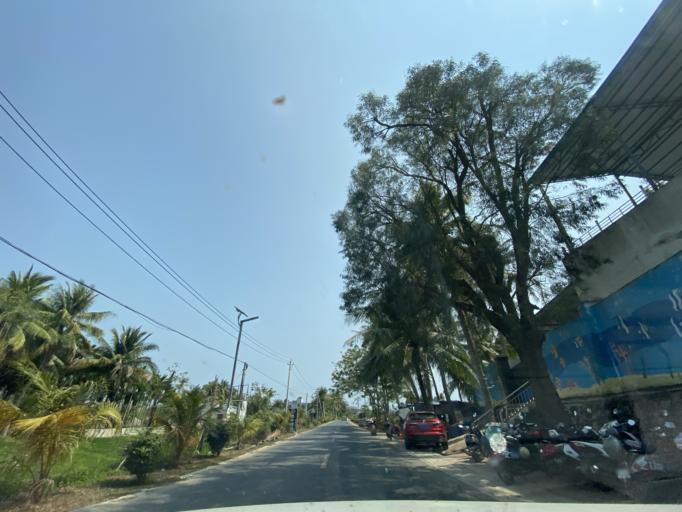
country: CN
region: Hainan
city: Yingzhou
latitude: 18.4193
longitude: 109.8130
